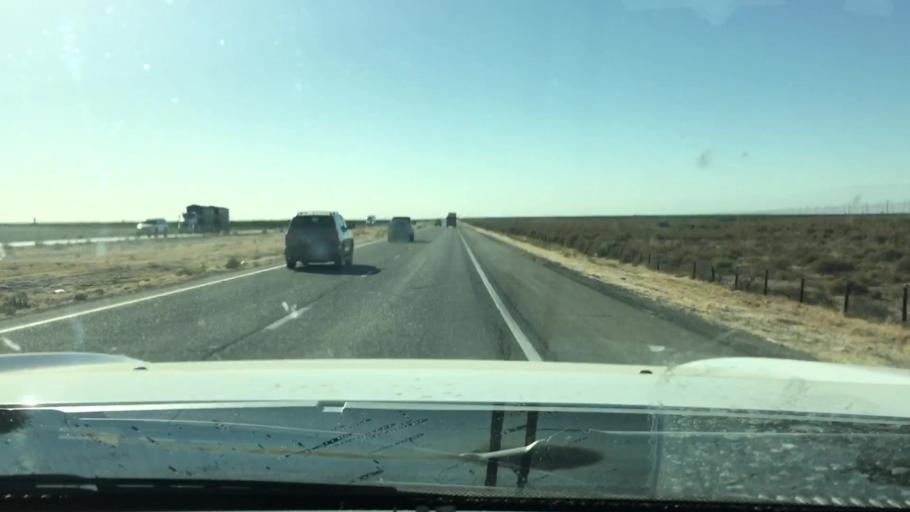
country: US
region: California
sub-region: Kern County
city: Buttonwillow
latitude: 35.4816
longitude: -119.5113
